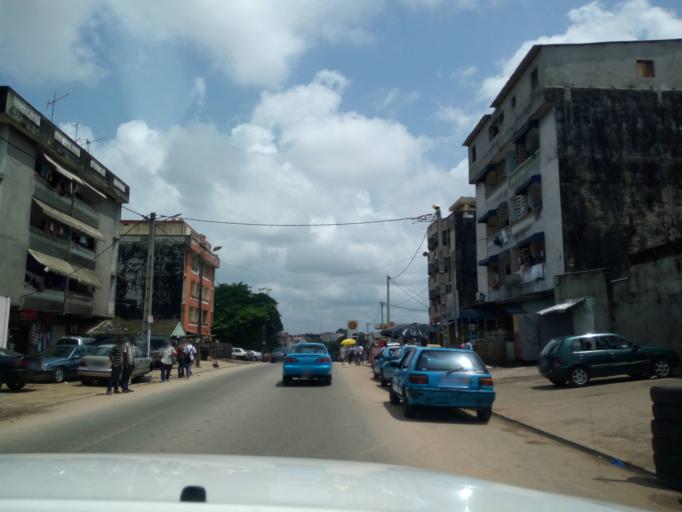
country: CI
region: Lagunes
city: Abidjan
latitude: 5.3394
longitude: -4.0908
